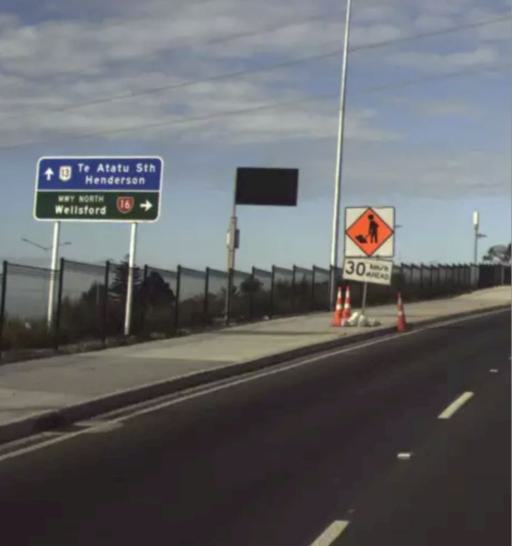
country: NZ
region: Auckland
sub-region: Auckland
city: Rosebank
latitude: -36.8564
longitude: 174.6519
